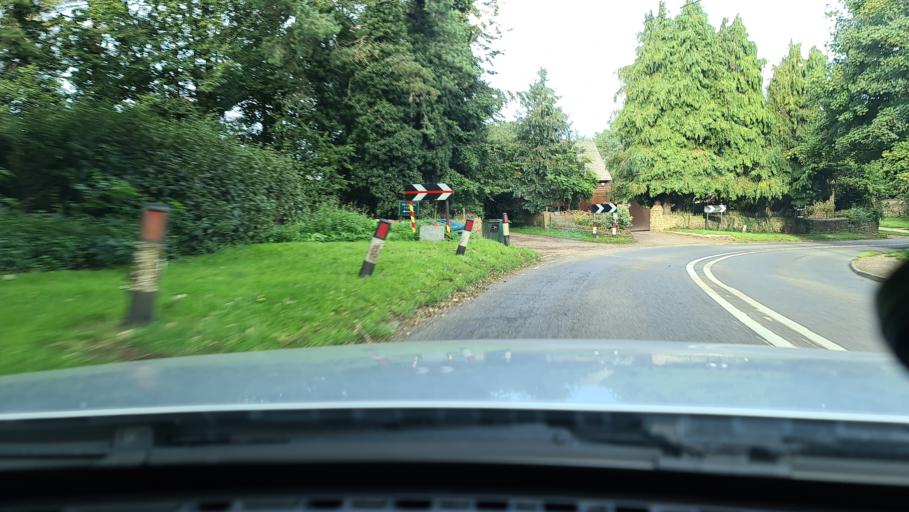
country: GB
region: England
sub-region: Oxfordshire
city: Hanwell
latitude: 52.0714
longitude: -1.3736
